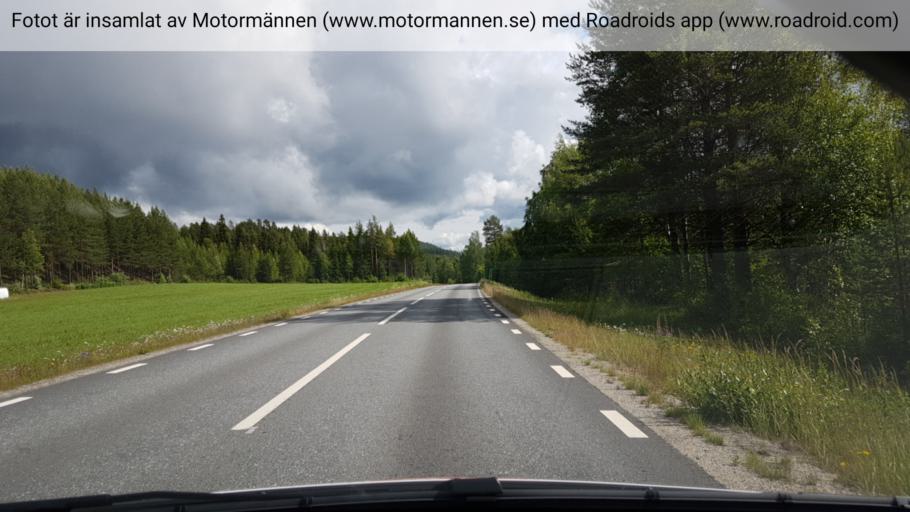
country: SE
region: Vaesterbotten
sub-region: Bjurholms Kommun
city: Bjurholm
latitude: 64.2806
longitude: 19.2396
